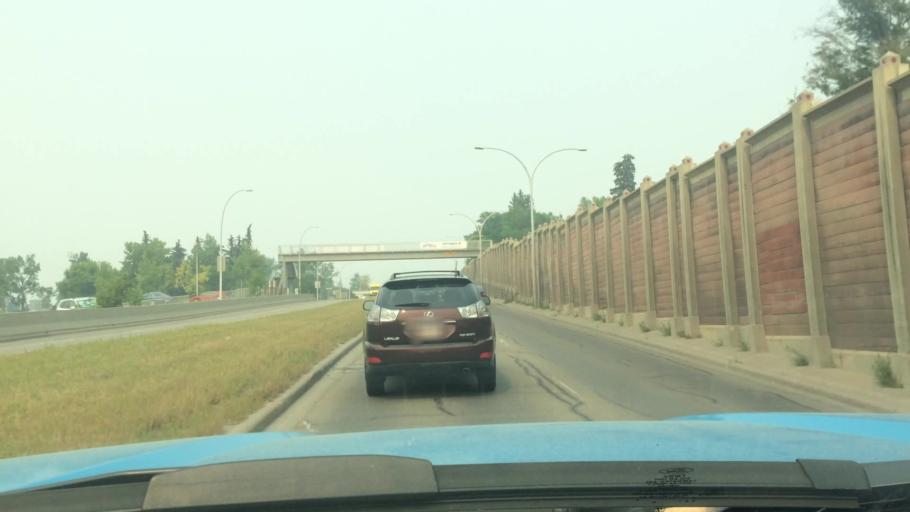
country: CA
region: Alberta
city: Calgary
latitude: 51.0641
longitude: -114.1179
